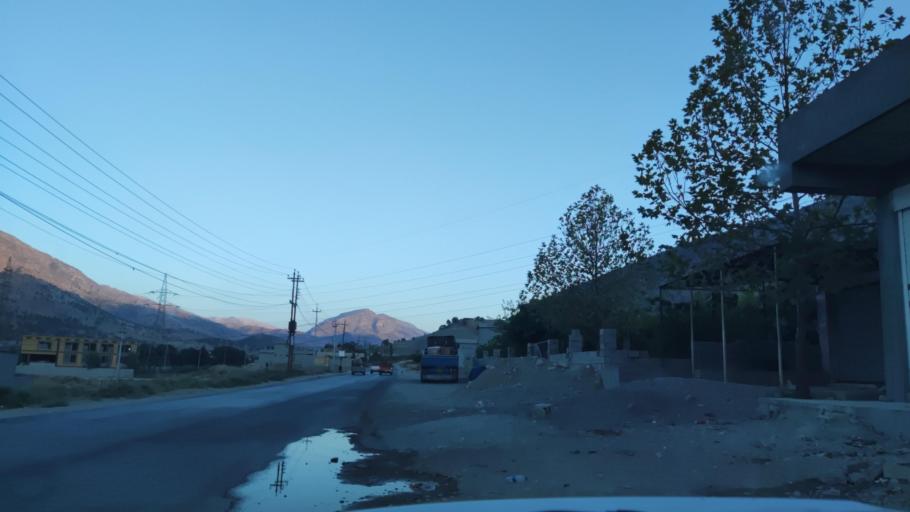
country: IQ
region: Arbil
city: Ruwandiz
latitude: 36.5868
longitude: 44.3953
